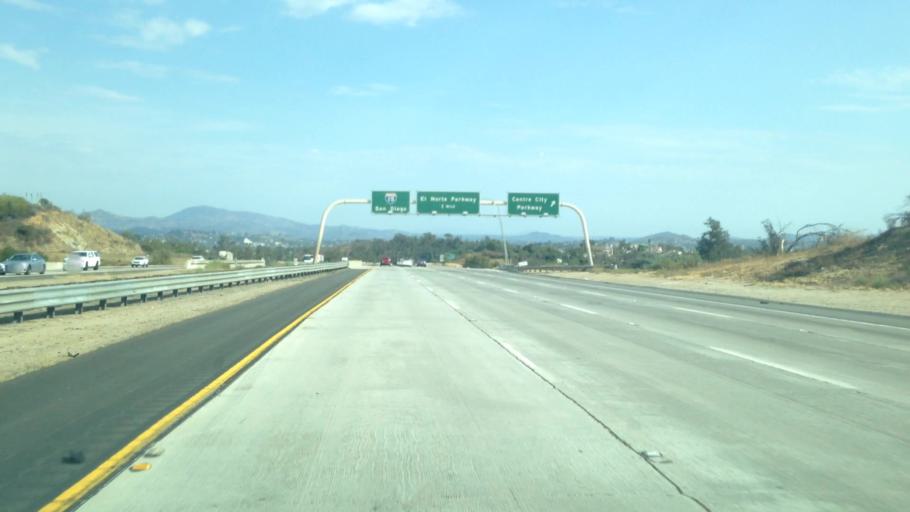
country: US
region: California
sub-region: San Diego County
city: Escondido
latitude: 33.1667
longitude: -117.1084
